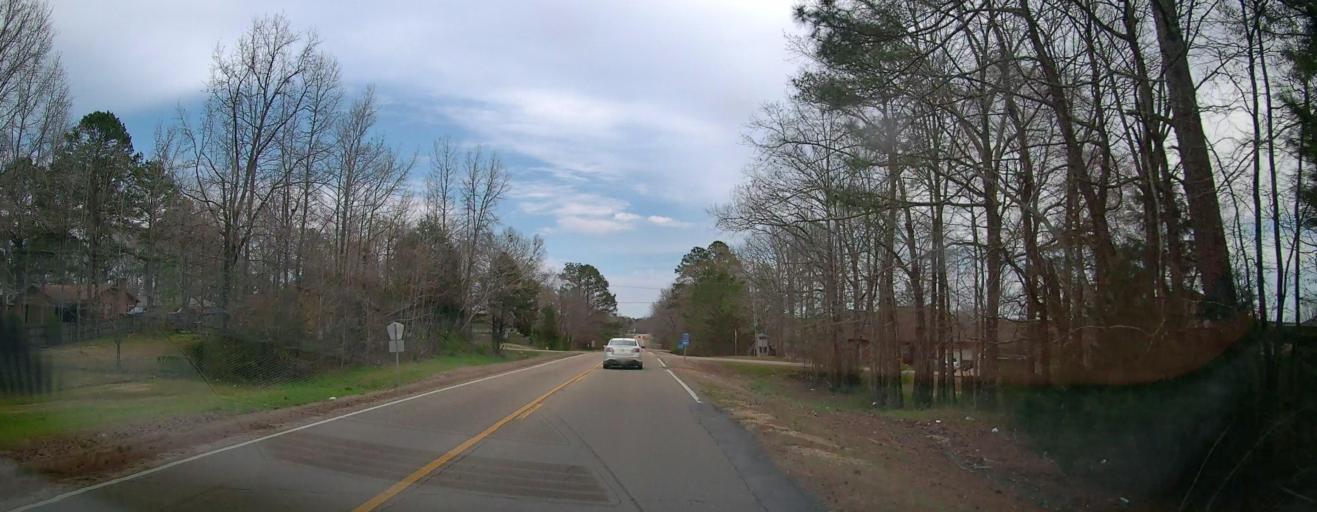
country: US
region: Mississippi
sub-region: Itawamba County
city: Mantachie
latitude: 34.2668
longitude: -88.5694
